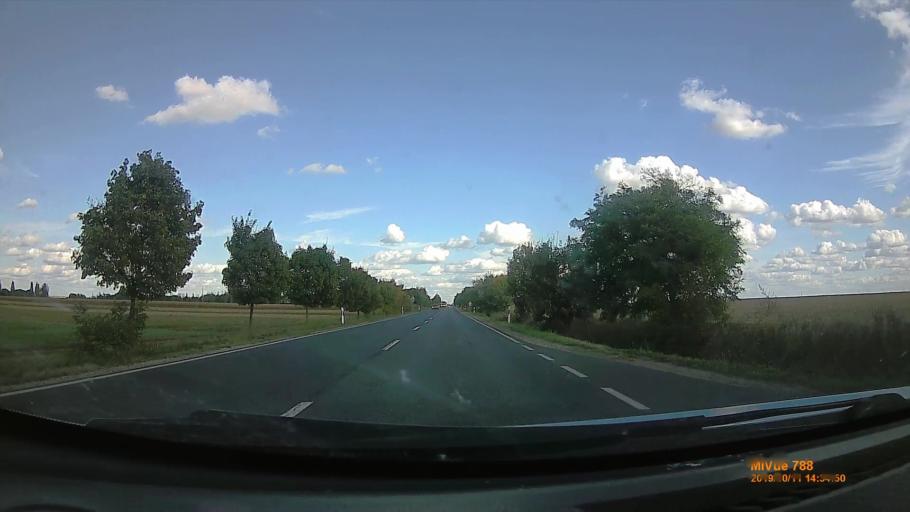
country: HU
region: Hajdu-Bihar
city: Ebes
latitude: 47.5600
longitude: 21.4820
